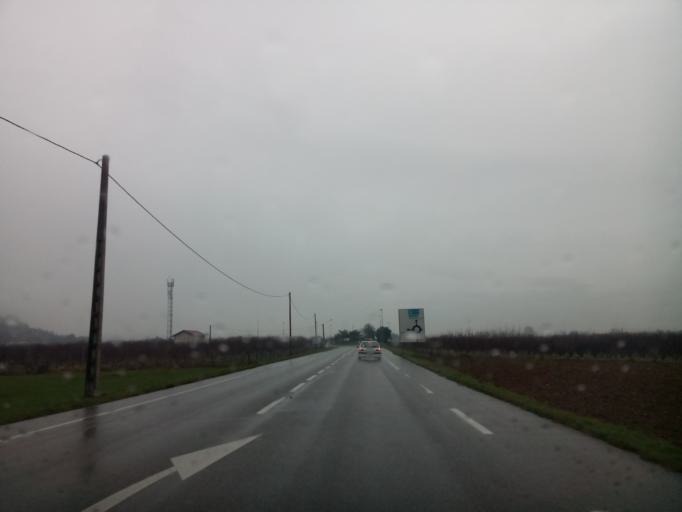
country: FR
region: Rhone-Alpes
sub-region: Departement de la Drome
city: Clerieux
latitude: 45.0540
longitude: 4.9608
